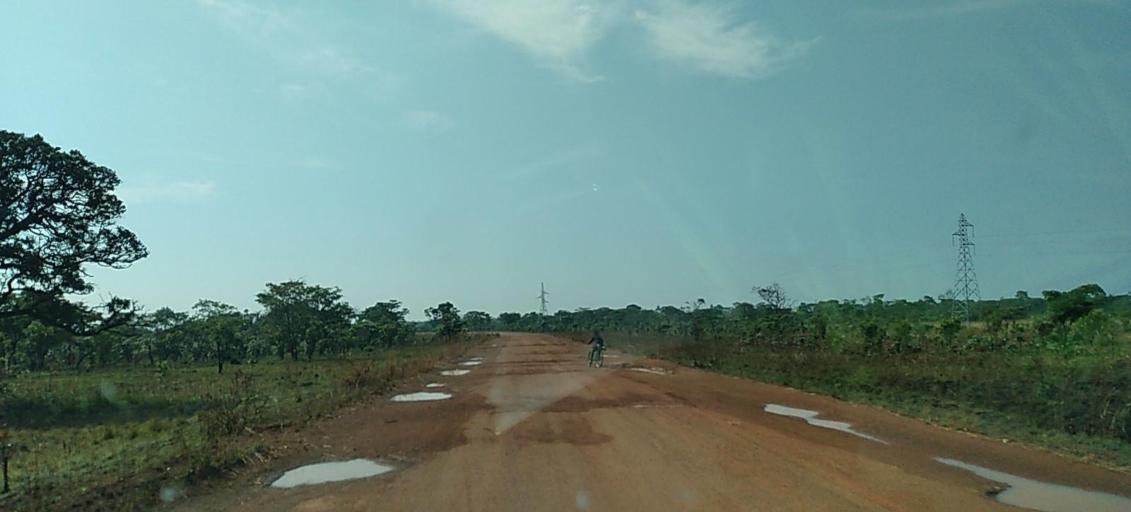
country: ZM
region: North-Western
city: Mwinilunga
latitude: -11.7837
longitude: 25.0253
